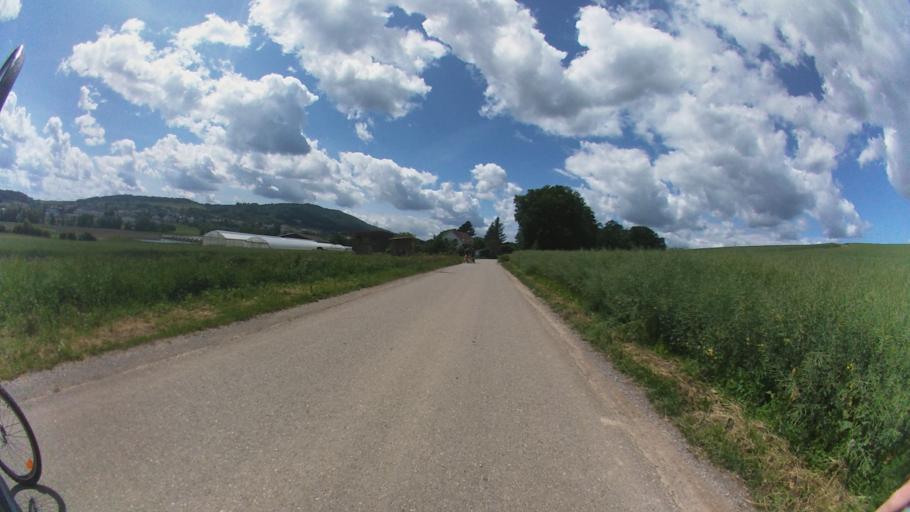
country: CH
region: Zurich
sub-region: Bezirk Dielsdorf
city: Steinmaur
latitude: 47.4940
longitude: 8.4661
